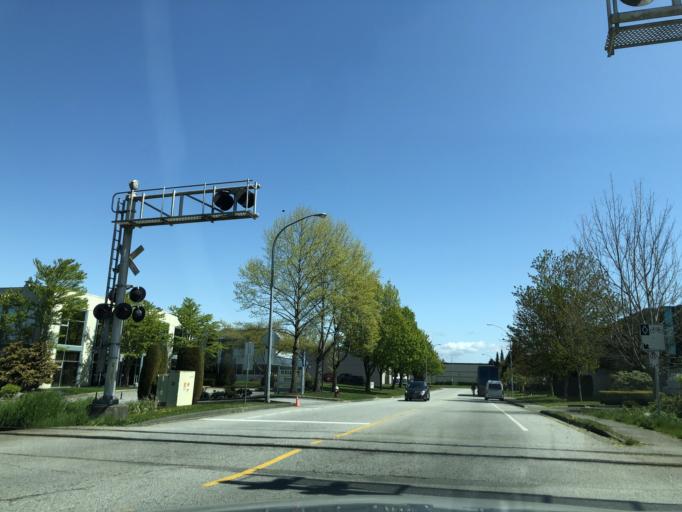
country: CA
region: British Columbia
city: Ladner
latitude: 49.1273
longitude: -123.1031
